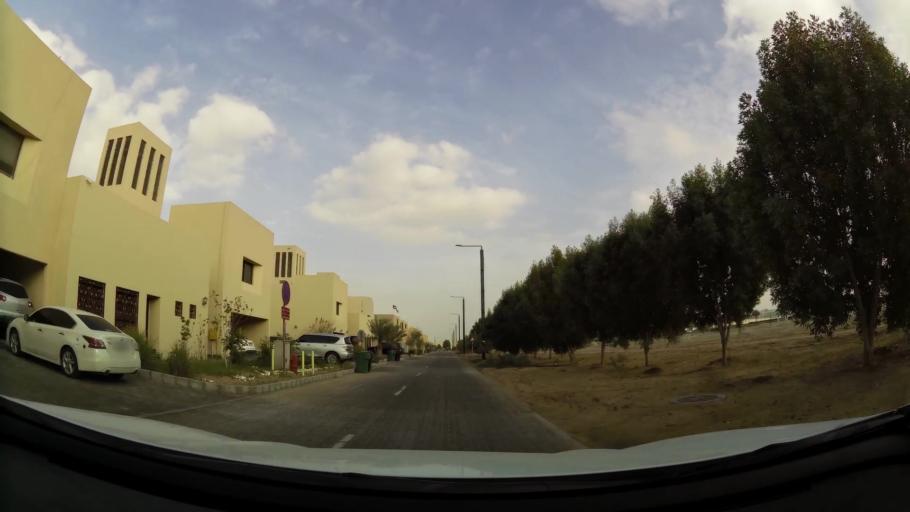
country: AE
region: Abu Dhabi
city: Abu Dhabi
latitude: 24.4995
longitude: 54.5991
